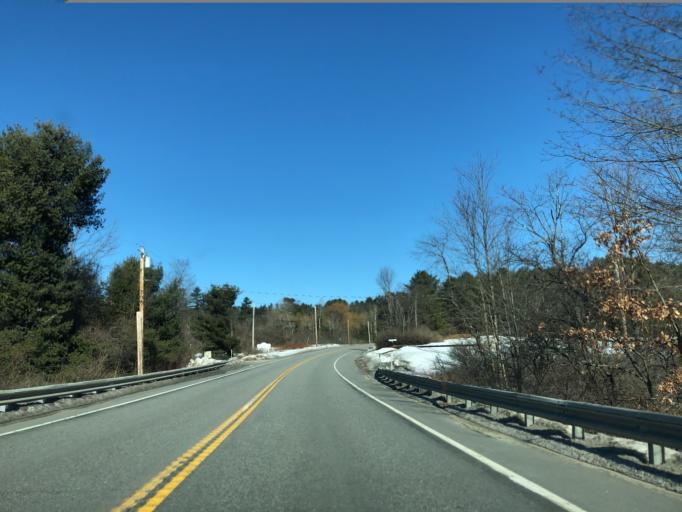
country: US
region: Maine
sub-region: Cumberland County
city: North Windham
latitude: 43.8467
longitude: -70.3845
